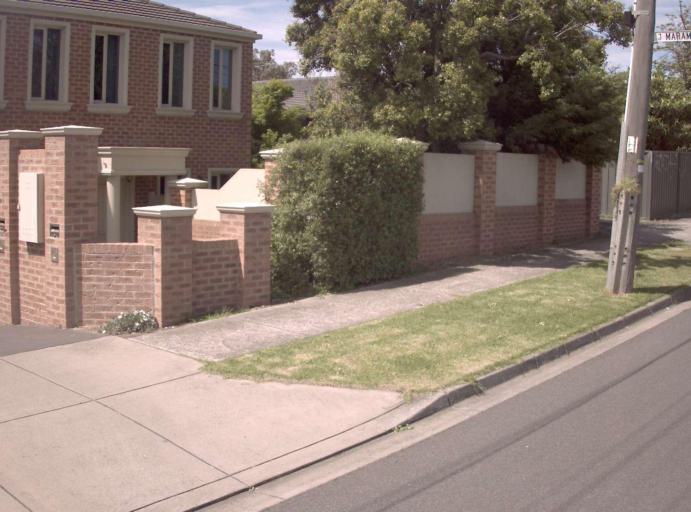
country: AU
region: Victoria
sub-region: Whitehorse
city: Blackburn South
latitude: -37.8395
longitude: 145.1557
